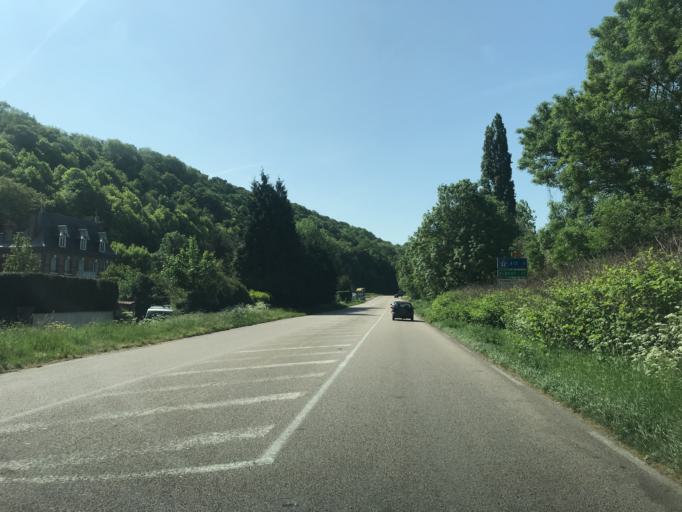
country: FR
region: Haute-Normandie
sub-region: Departement de la Seine-Maritime
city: Les Authieux-sur-le-Port-Saint-Ouen
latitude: 49.3512
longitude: 1.1277
